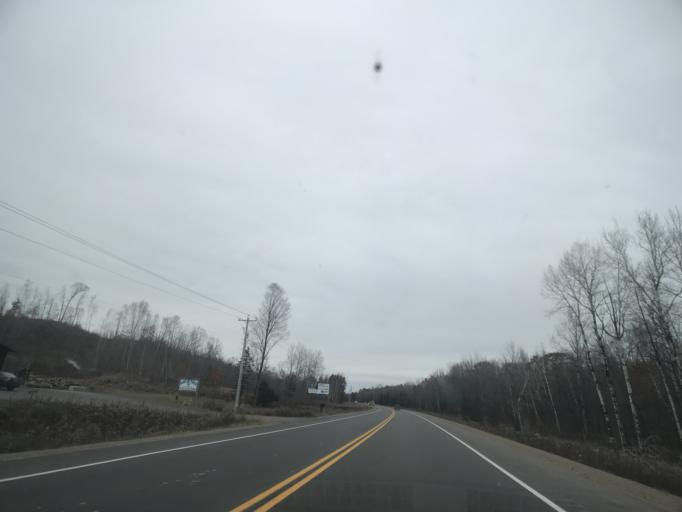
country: US
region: Wisconsin
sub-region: Menominee County
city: Legend Lake
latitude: 45.2904
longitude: -88.5106
